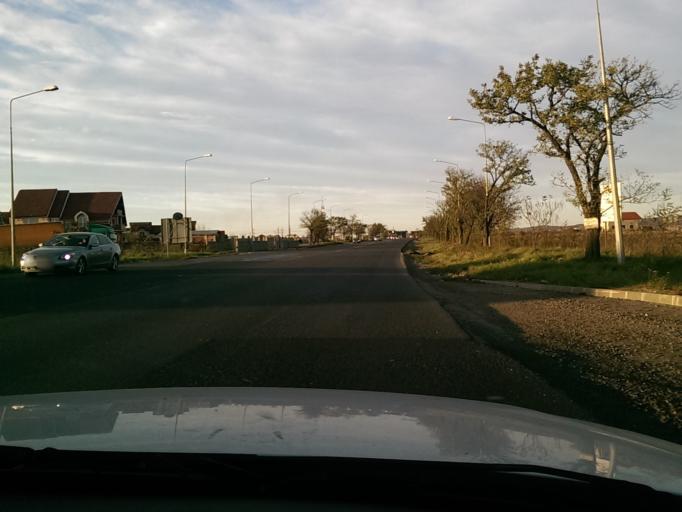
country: RO
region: Bihor
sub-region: Comuna Sanmartin
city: Sanmartin
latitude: 47.0160
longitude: 21.9642
